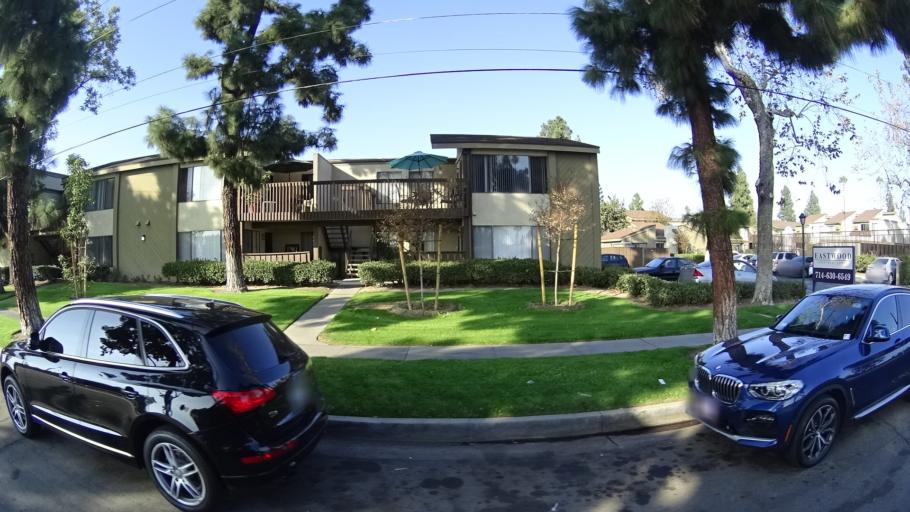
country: US
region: California
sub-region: Orange County
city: Placentia
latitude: 33.8448
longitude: -117.8636
